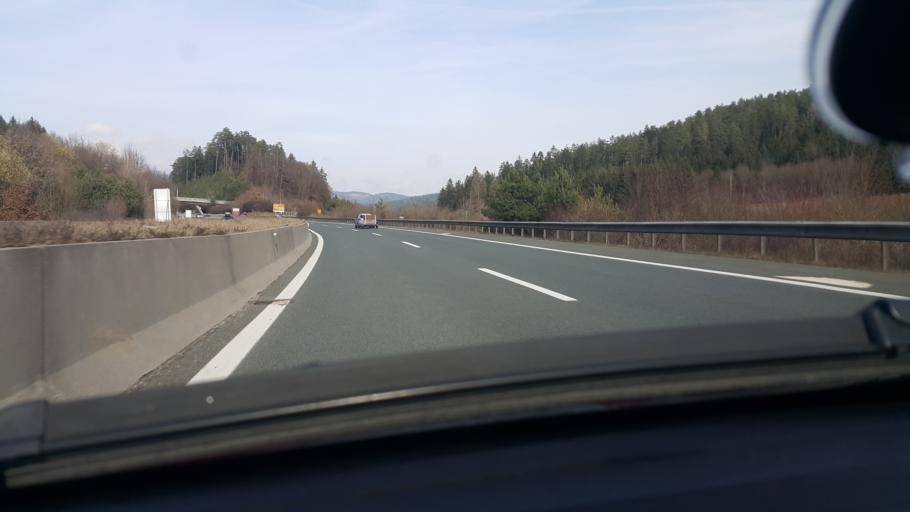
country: AT
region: Carinthia
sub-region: Politischer Bezirk Volkermarkt
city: Voelkermarkt
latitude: 46.6469
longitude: 14.5596
